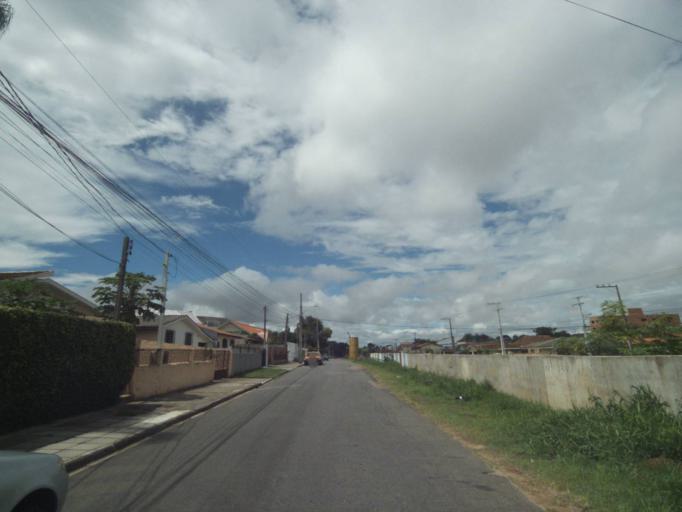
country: BR
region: Parana
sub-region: Curitiba
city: Curitiba
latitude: -25.4844
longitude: -49.2779
